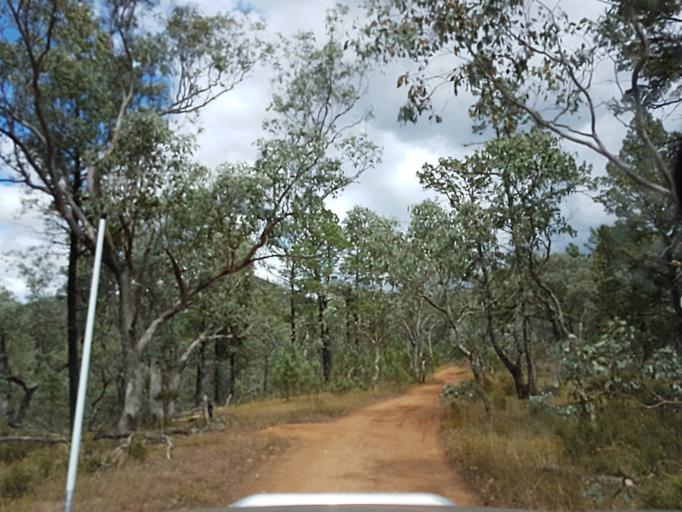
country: AU
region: New South Wales
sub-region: Snowy River
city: Jindabyne
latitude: -36.9300
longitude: 148.3943
